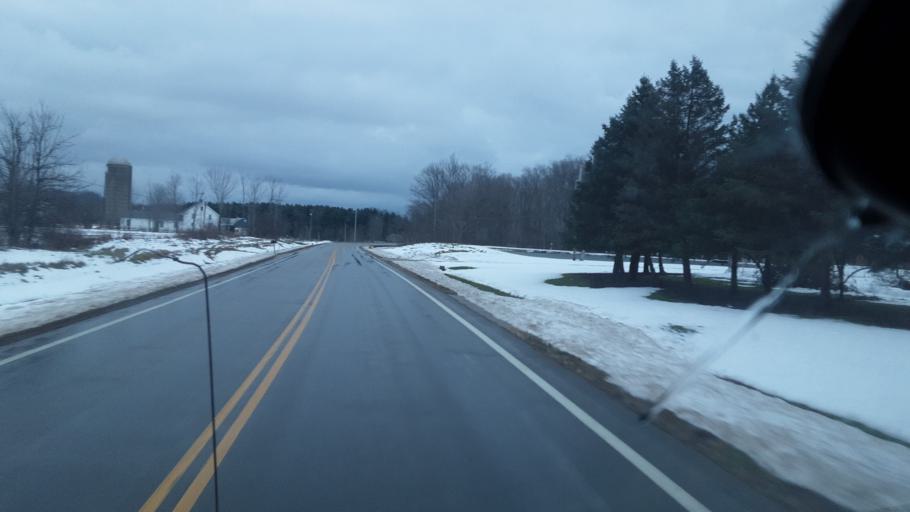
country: US
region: Ohio
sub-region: Ashtabula County
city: Jefferson
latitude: 41.7122
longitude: -80.7301
